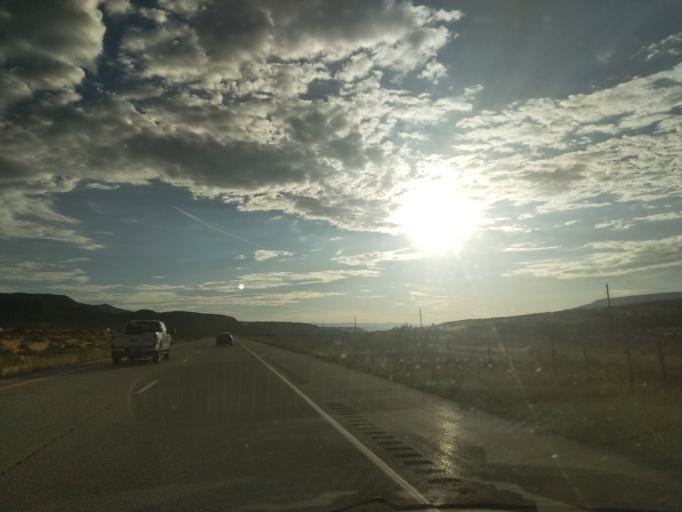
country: US
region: Colorado
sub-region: Garfield County
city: Battlement Mesa
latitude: 39.4886
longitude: -107.9558
